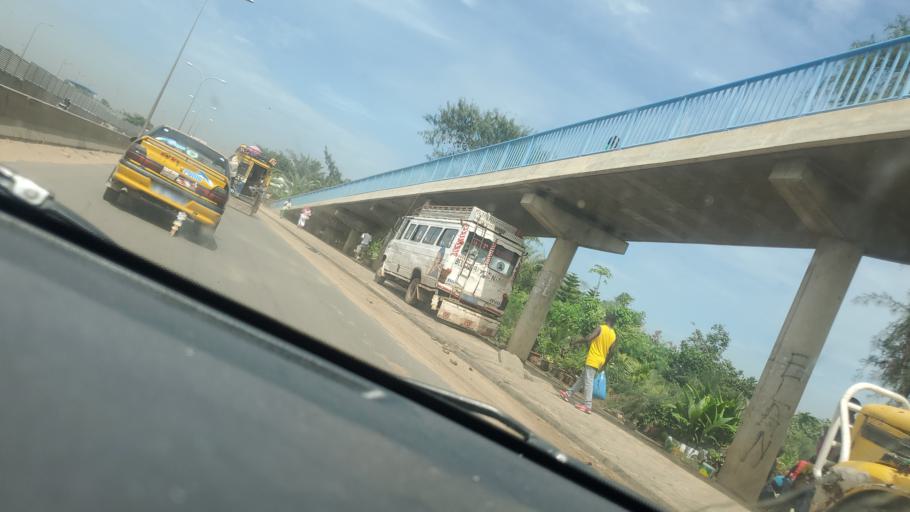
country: SN
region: Dakar
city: Grand Dakar
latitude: 14.7430
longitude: -17.4334
